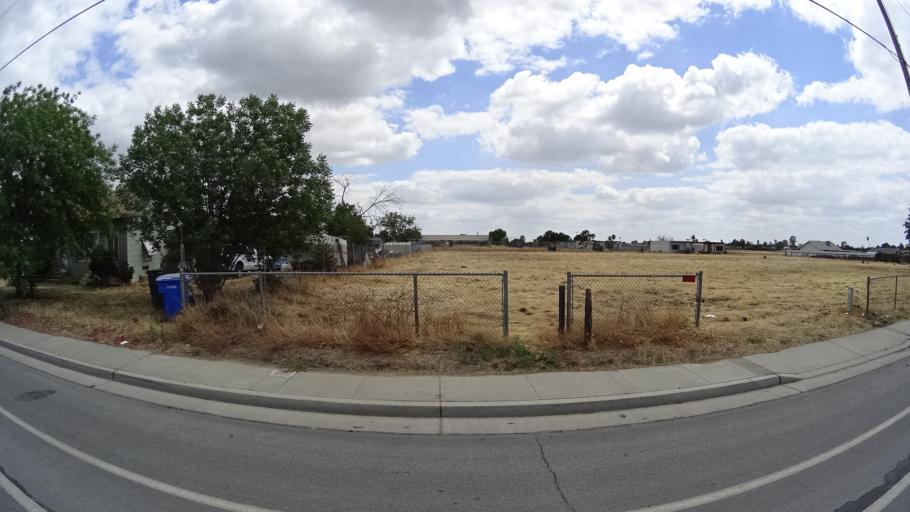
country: US
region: California
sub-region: Kings County
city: Hanford
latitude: 36.3134
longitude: -119.6466
